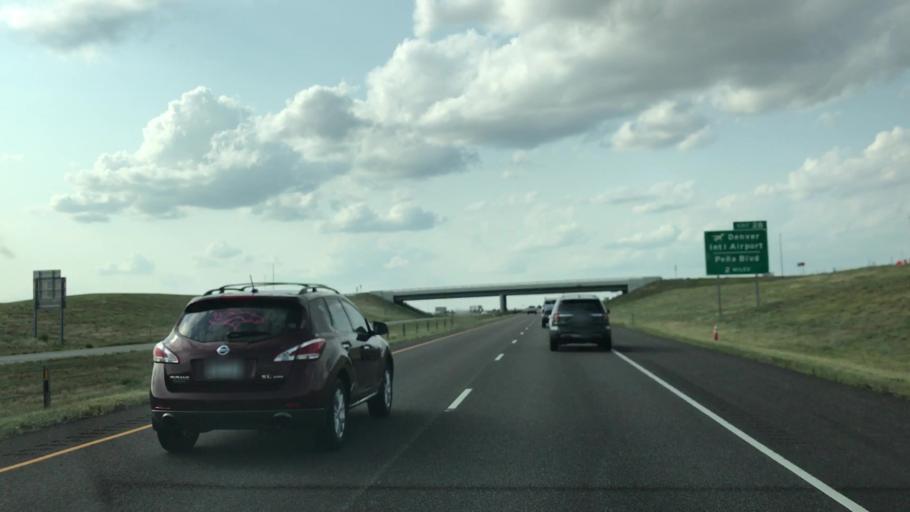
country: US
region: Colorado
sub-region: Adams County
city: Aurora
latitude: 39.8107
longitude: -104.7194
